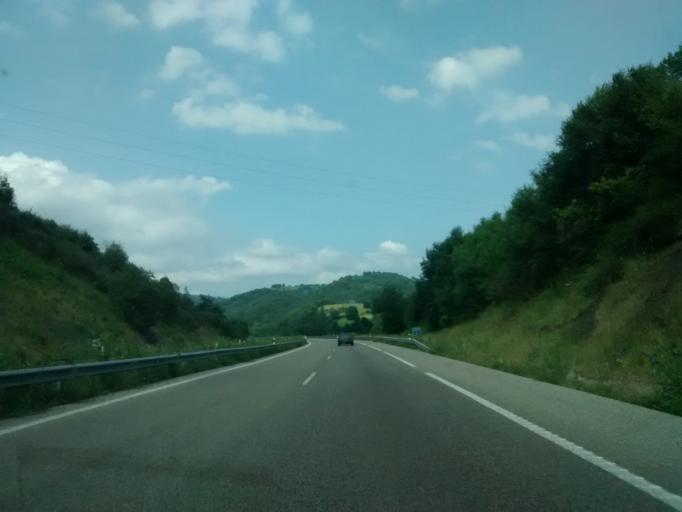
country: ES
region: Asturias
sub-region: Province of Asturias
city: Mieres
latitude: 43.2980
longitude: -5.7542
